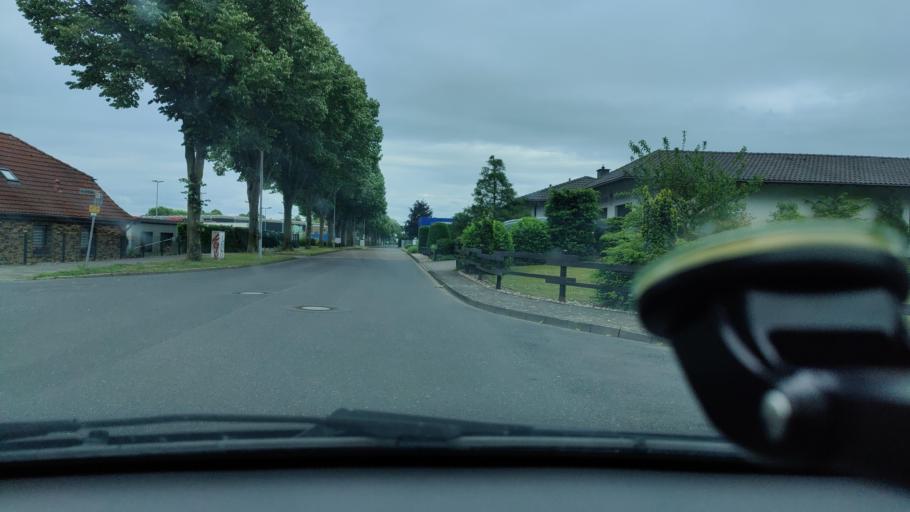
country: DE
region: North Rhine-Westphalia
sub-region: Regierungsbezirk Dusseldorf
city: Xanten
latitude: 51.6556
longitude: 6.4329
